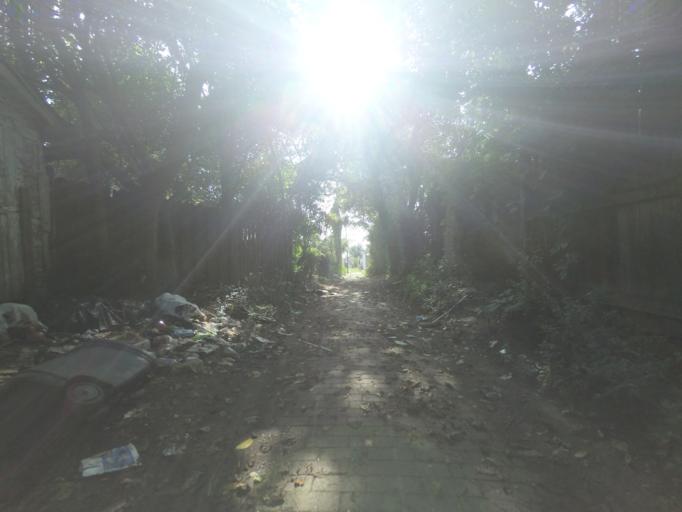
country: US
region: West Virginia
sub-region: Cabell County
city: Huntington
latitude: 38.4271
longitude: -82.4049
